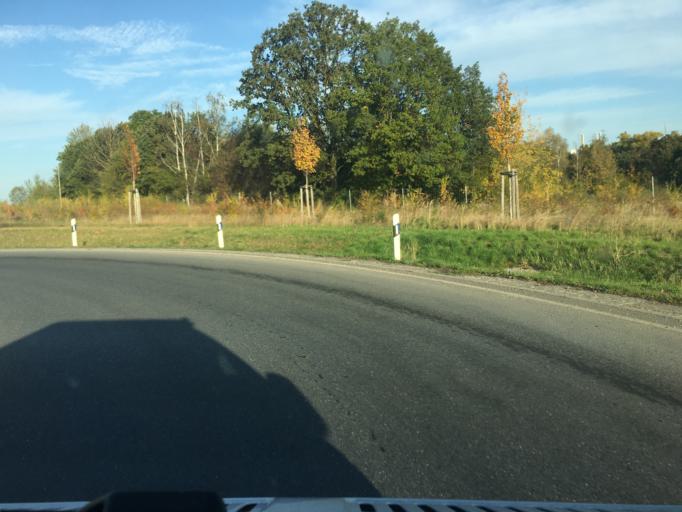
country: DE
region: Saxony
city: Neukirchen
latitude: 50.8036
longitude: 12.3739
